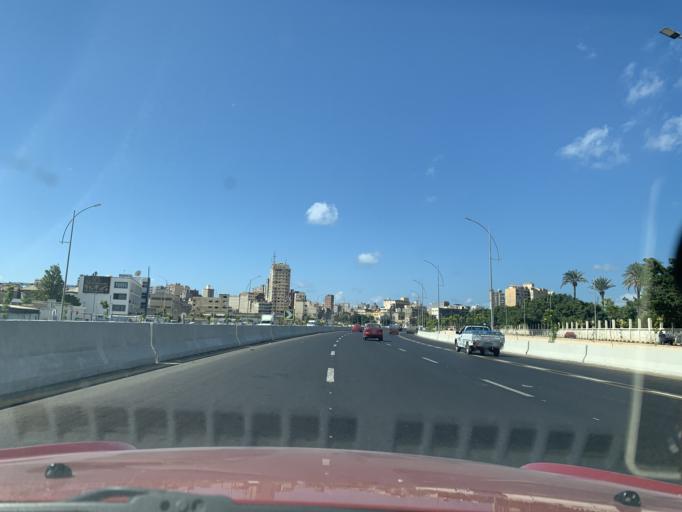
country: EG
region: Alexandria
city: Alexandria
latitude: 31.2006
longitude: 29.9465
